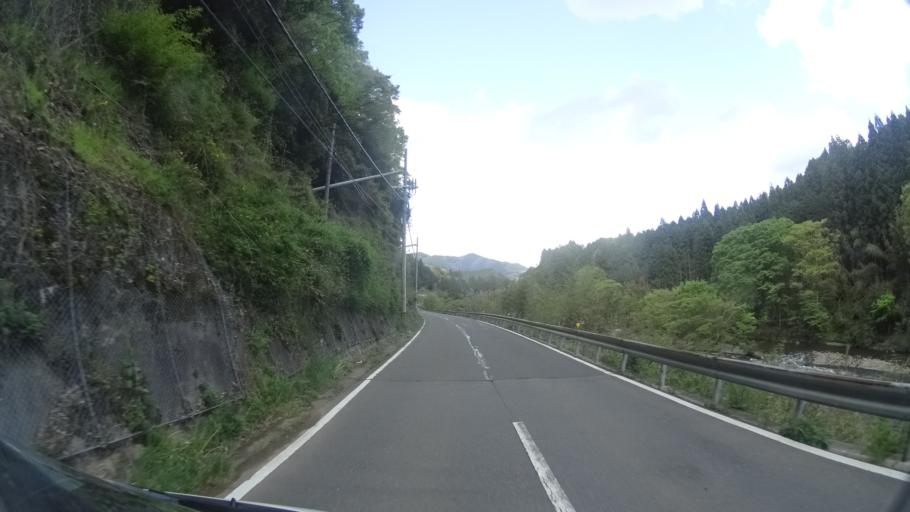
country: JP
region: Kyoto
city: Ayabe
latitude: 35.2701
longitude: 135.3718
